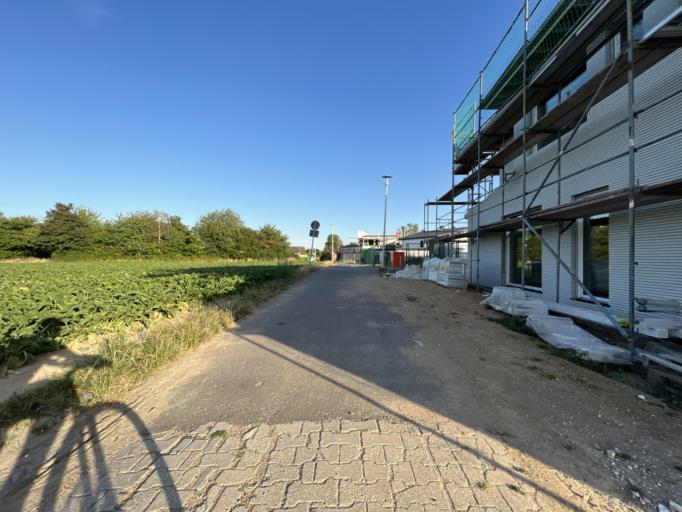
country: DE
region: North Rhine-Westphalia
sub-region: Regierungsbezirk Koln
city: Dueren
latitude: 50.7782
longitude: 6.4466
